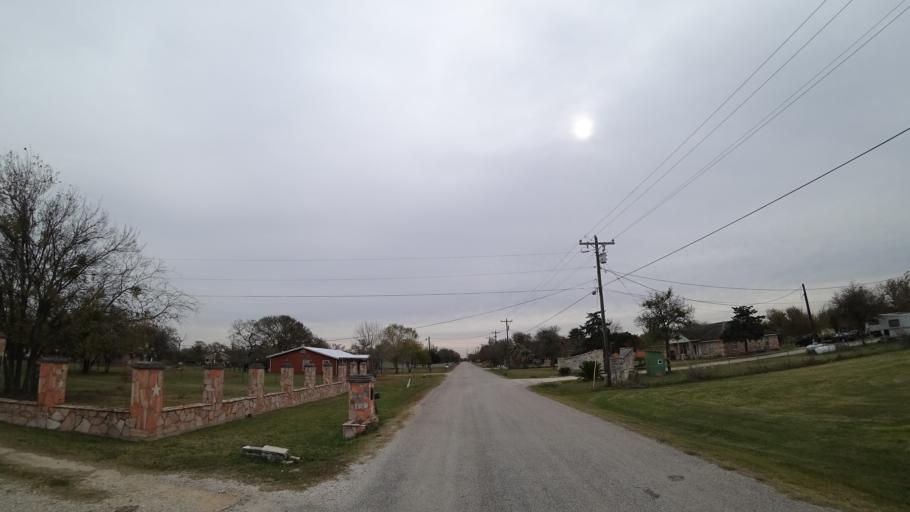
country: US
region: Texas
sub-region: Travis County
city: Garfield
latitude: 30.1082
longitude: -97.5760
